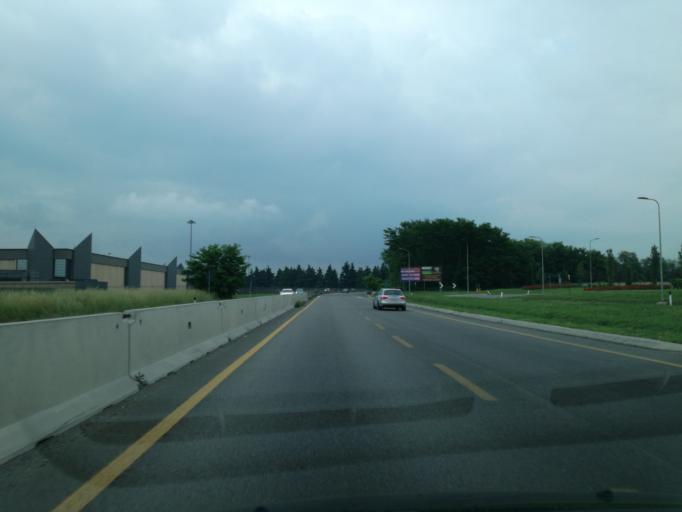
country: IT
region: Lombardy
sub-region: Provincia di Monza e Brianza
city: Villasanta
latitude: 45.5930
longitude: 9.3115
